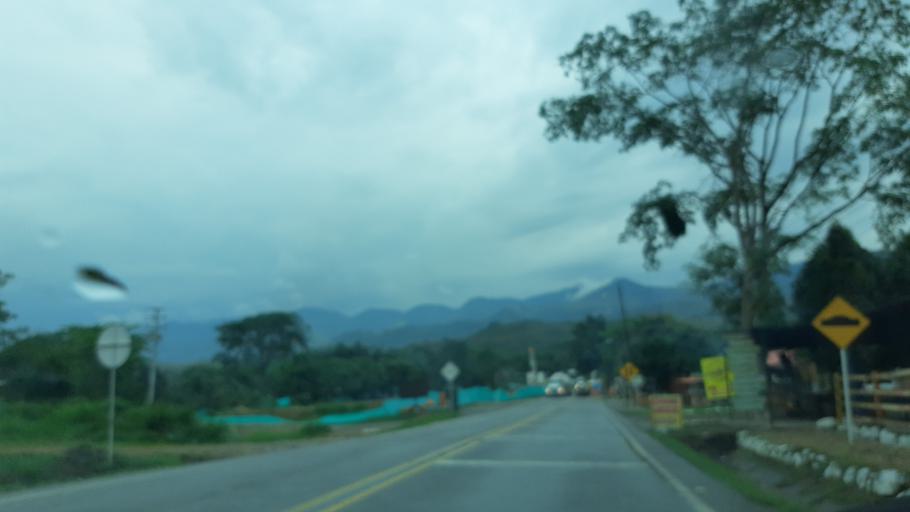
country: CO
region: Casanare
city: Monterrey
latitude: 4.8850
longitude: -72.8986
